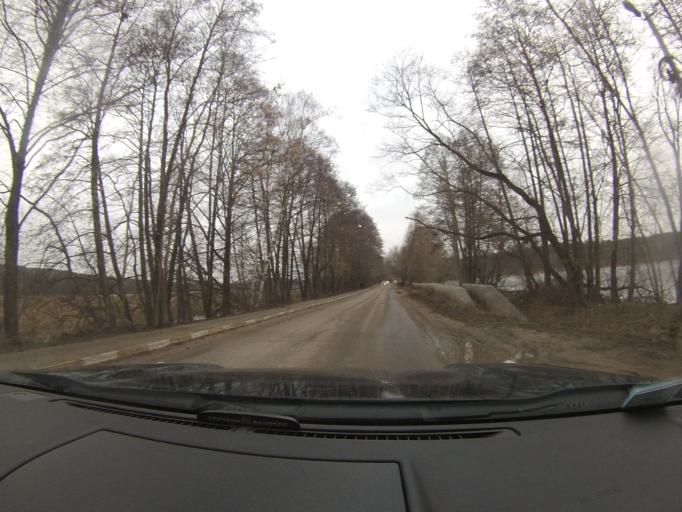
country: RU
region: Moskovskaya
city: Peski
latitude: 55.2625
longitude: 38.7615
